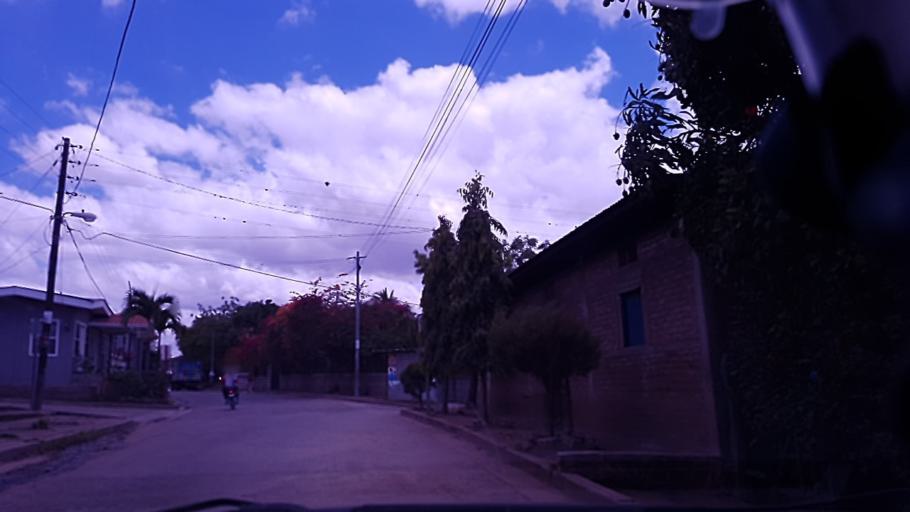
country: NI
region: Esteli
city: Condega
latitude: 13.3667
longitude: -86.3982
